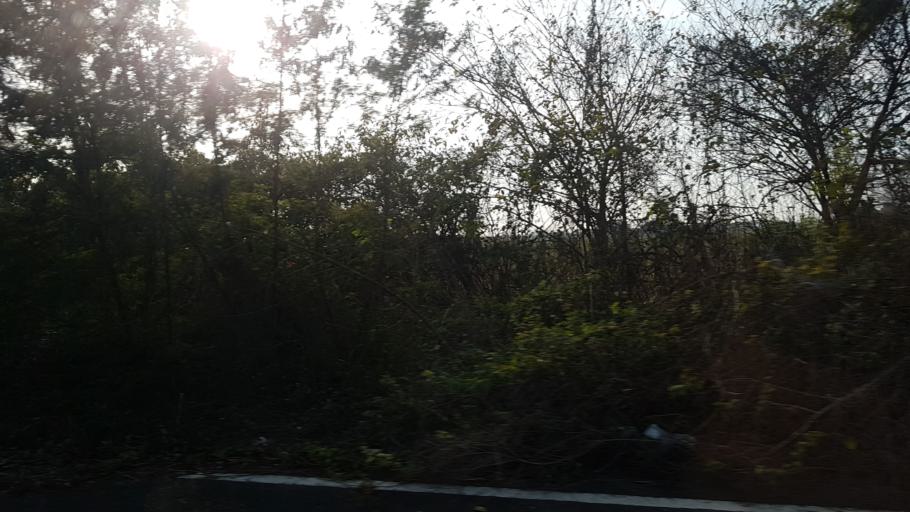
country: TW
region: Taiwan
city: Xinying
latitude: 23.3473
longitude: 120.3740
